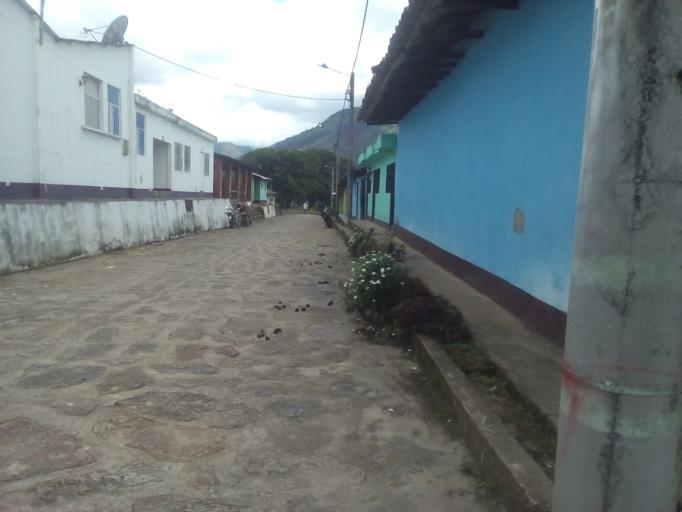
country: CO
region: Casanare
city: Nunchia
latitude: 5.6247
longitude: -72.4238
